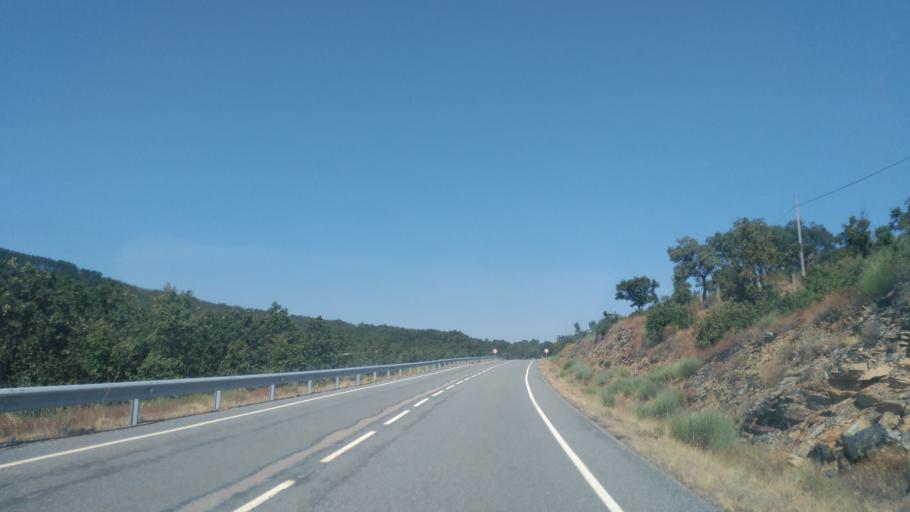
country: ES
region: Castille and Leon
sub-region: Provincia de Salamanca
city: Cereceda de la Sierra
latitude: 40.5860
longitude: -6.0867
